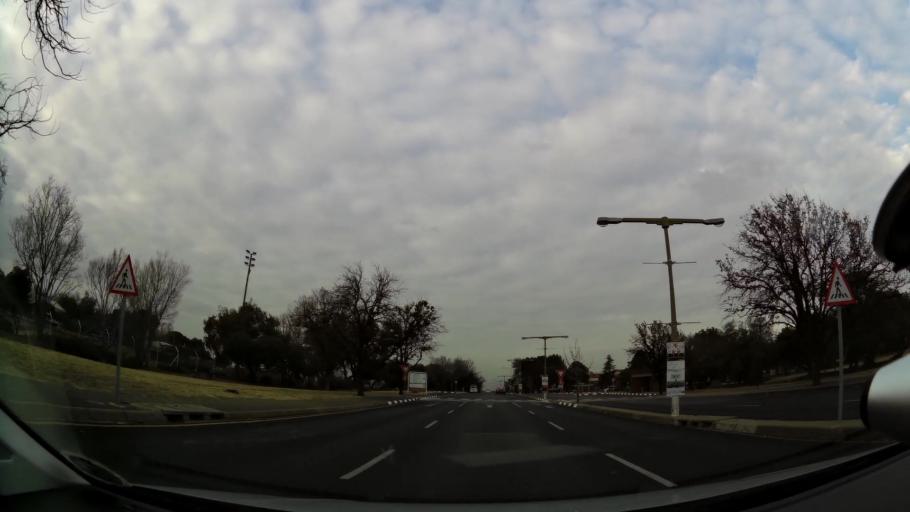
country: ZA
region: Orange Free State
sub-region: Mangaung Metropolitan Municipality
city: Bloemfontein
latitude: -29.1088
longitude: 26.1922
